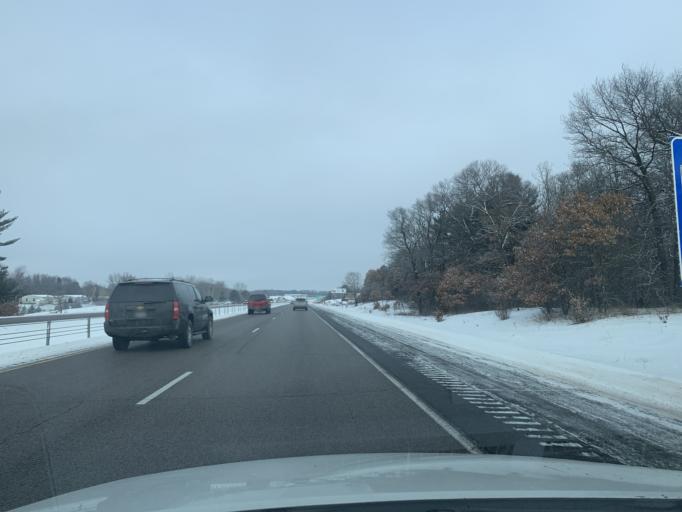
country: US
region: Minnesota
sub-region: Chisago County
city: Stacy
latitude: 45.3880
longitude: -92.9921
